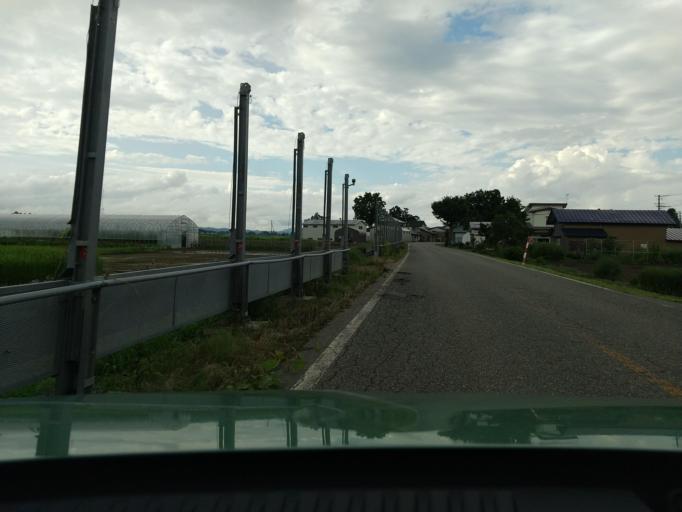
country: JP
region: Akita
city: Yokotemachi
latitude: 39.3109
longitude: 140.4895
